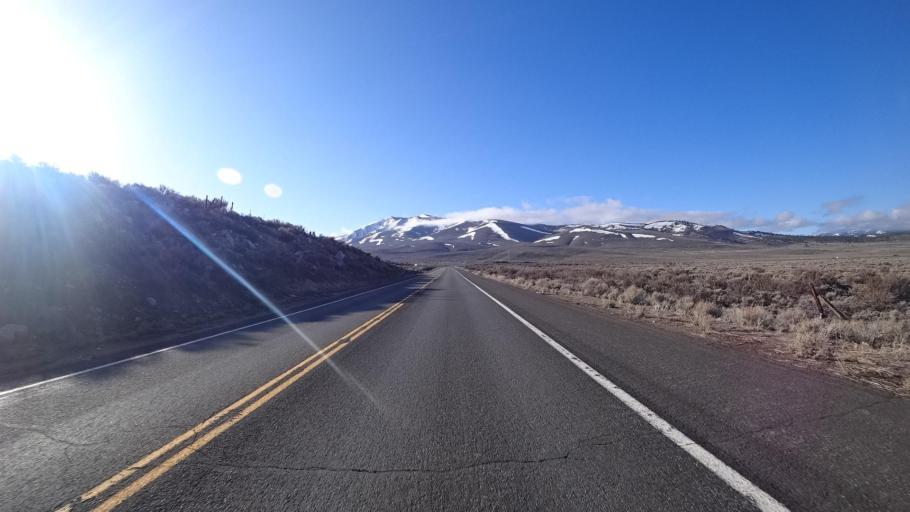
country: US
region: Nevada
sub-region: Washoe County
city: Cold Springs
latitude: 39.6485
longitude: -119.9592
